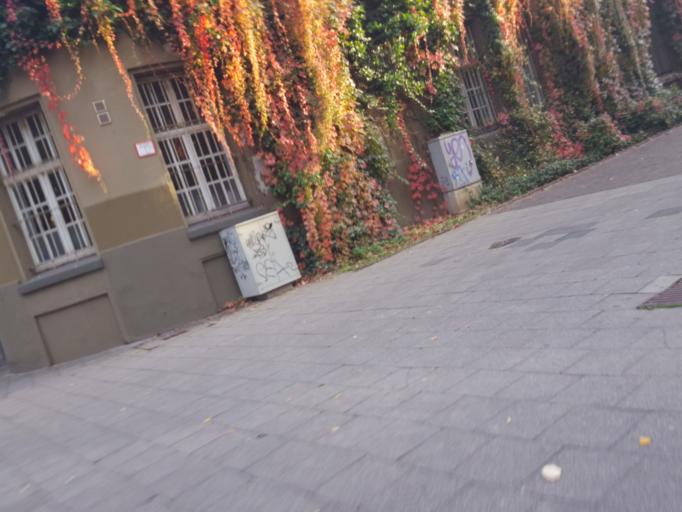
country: DE
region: North Rhine-Westphalia
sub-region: Regierungsbezirk Dusseldorf
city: Essen
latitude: 51.4550
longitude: 7.0105
